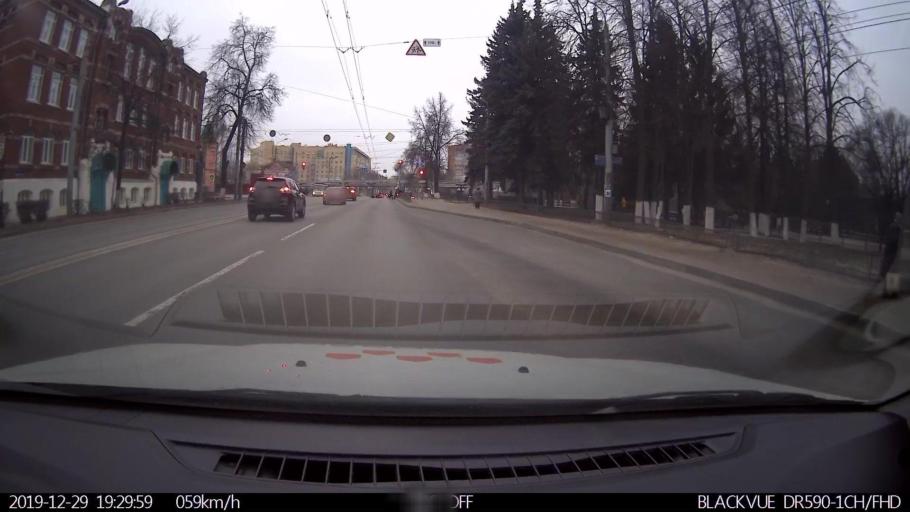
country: RU
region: Nizjnij Novgorod
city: Neklyudovo
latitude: 56.3571
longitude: 43.8649
